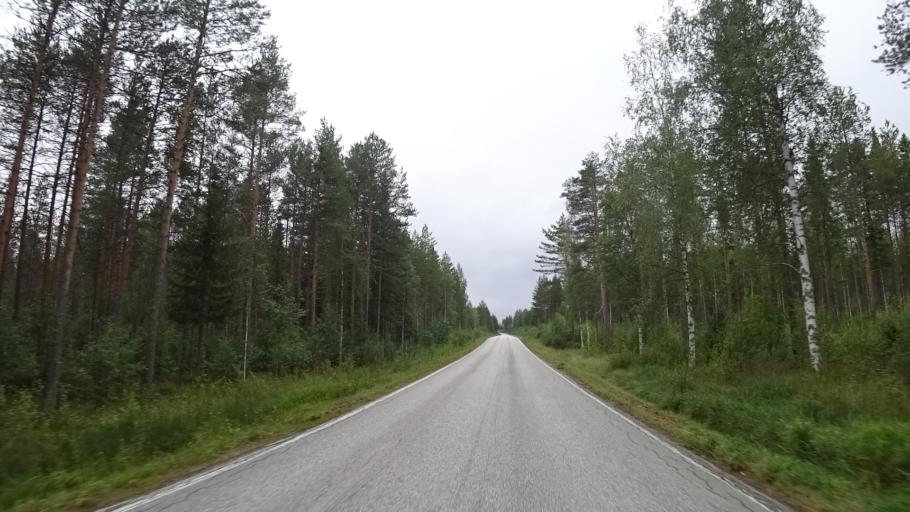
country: FI
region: North Karelia
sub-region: Pielisen Karjala
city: Lieksa
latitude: 63.3724
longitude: 30.3006
